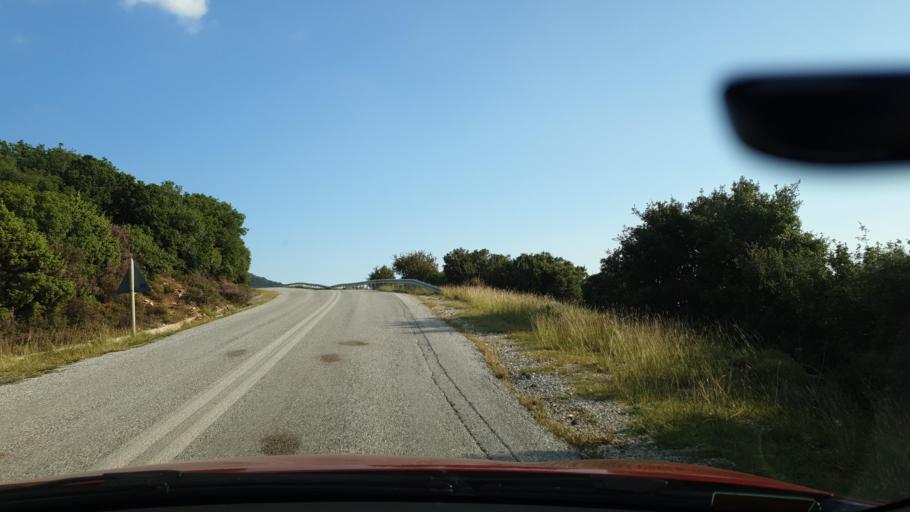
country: GR
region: Central Macedonia
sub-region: Nomos Thessalonikis
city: Peristera
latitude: 40.5218
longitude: 23.2016
